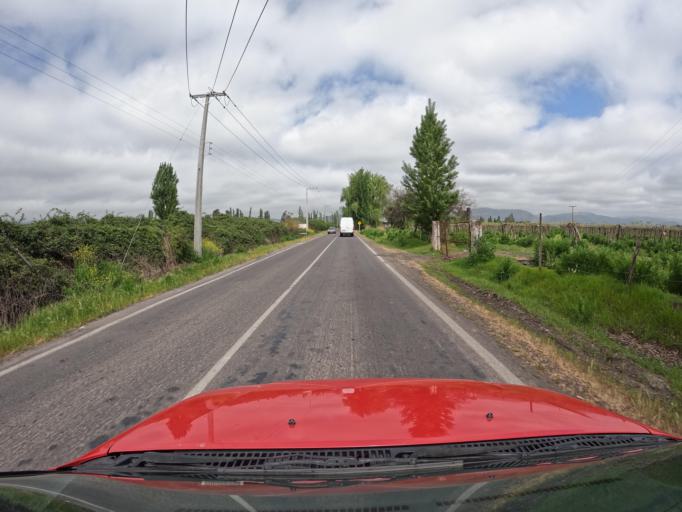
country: CL
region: O'Higgins
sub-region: Provincia de Colchagua
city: Santa Cruz
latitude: -34.6775
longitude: -71.3580
